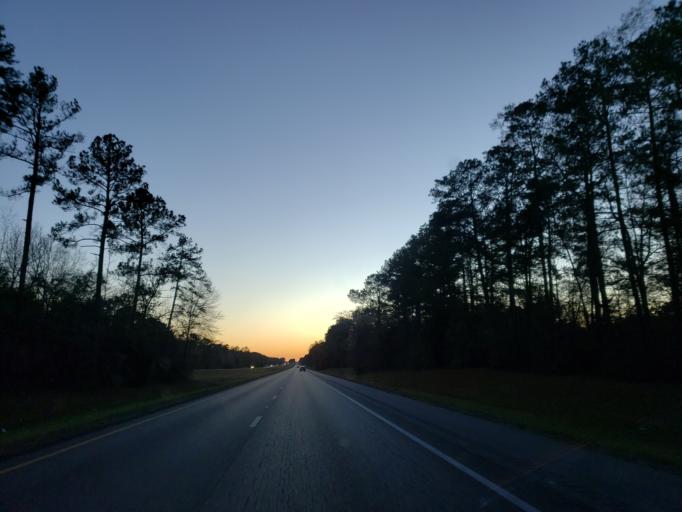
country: US
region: Mississippi
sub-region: Jones County
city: Sharon
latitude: 31.7581
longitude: -89.0667
